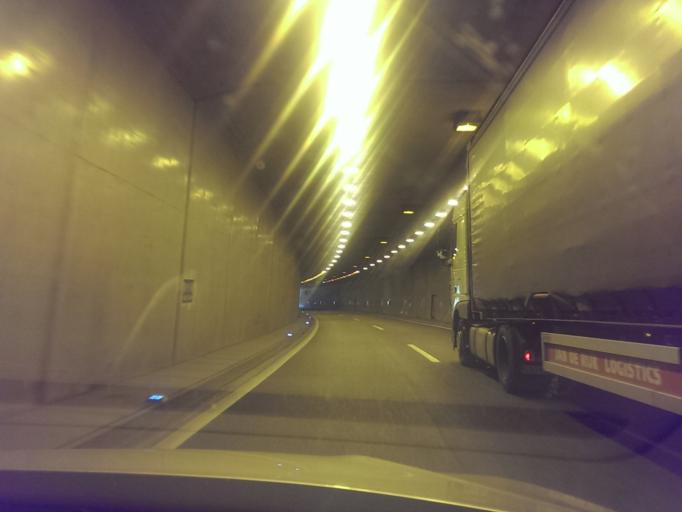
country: AT
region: Upper Austria
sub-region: Politischer Bezirk Kirchdorf an der Krems
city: Micheldorf in Oberoesterreich
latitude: 47.8673
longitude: 14.1405
